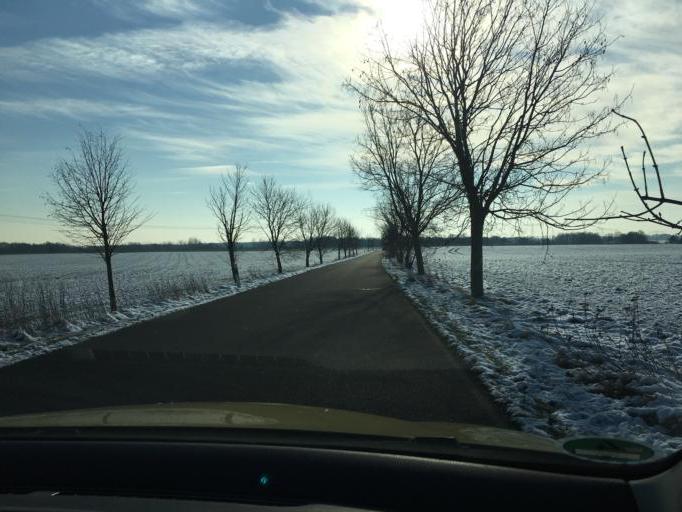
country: DE
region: Saxony
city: Belgershain
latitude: 51.2243
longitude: 12.5548
